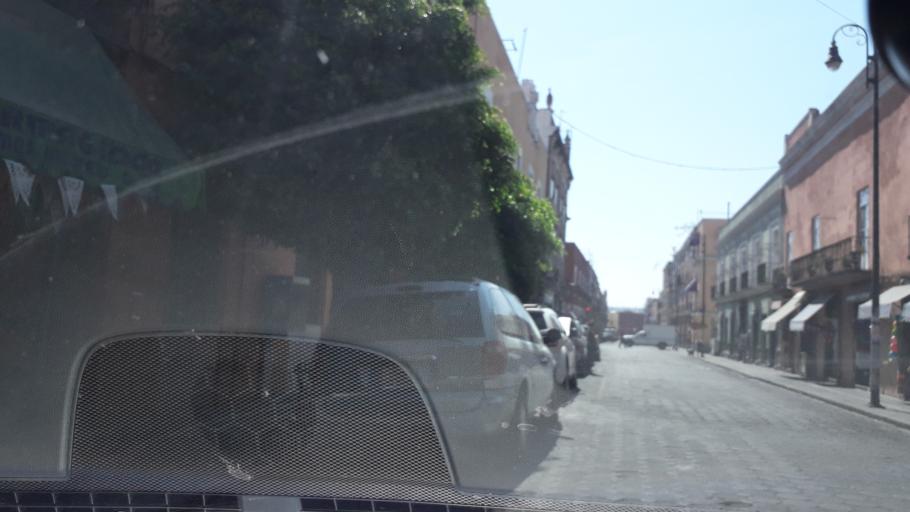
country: MX
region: Puebla
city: Puebla
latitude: 19.0463
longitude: -98.1945
